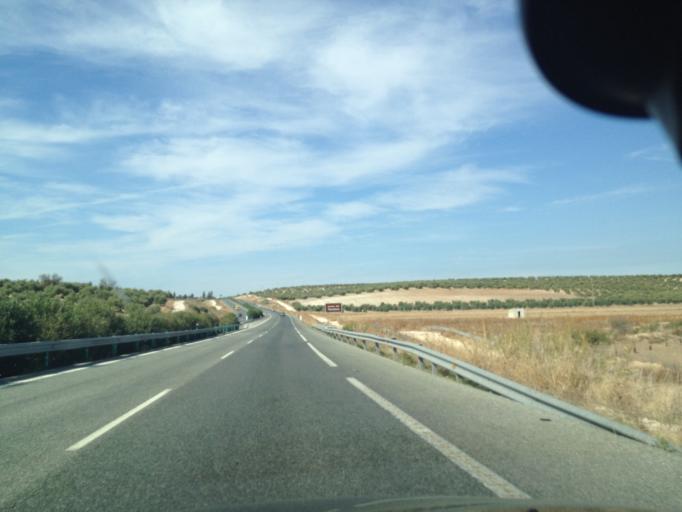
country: ES
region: Andalusia
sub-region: Provincia de Sevilla
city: La Puebla de Cazalla
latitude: 37.2313
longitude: -5.2421
